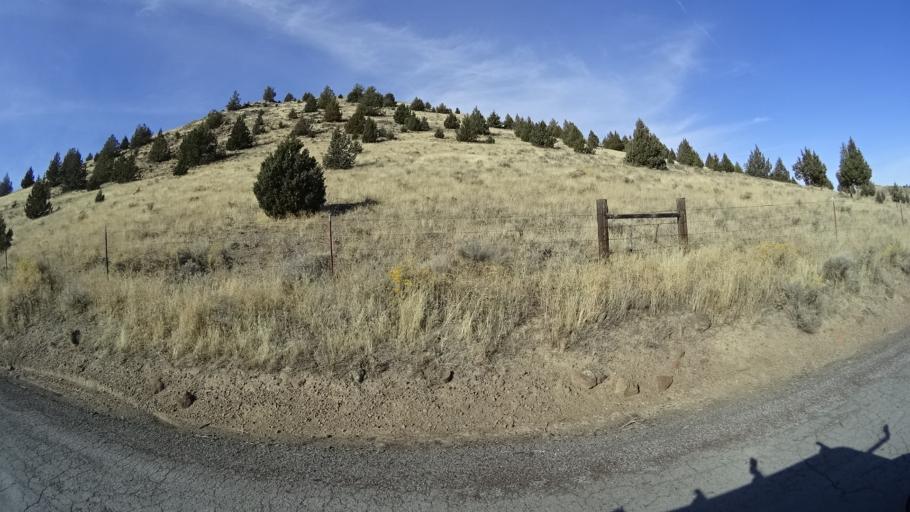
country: US
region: California
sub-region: Siskiyou County
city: Weed
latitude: 41.5570
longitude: -122.4720
